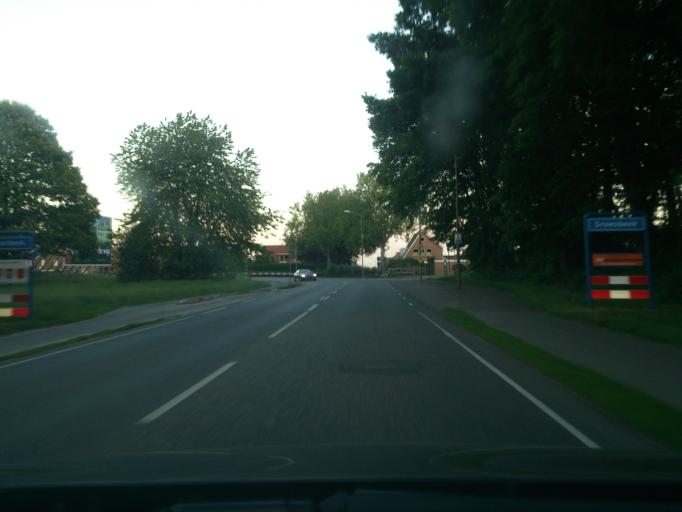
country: NL
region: Gelderland
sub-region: Gemeente Groesbeek
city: Groesbeek
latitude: 51.7885
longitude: 5.9168
